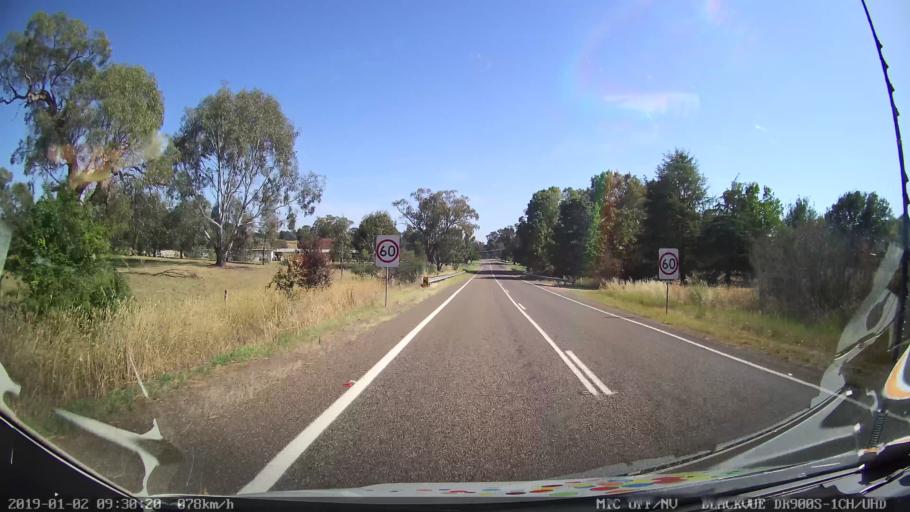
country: AU
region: New South Wales
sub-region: Tumut Shire
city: Tumut
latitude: -35.3278
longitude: 148.2376
